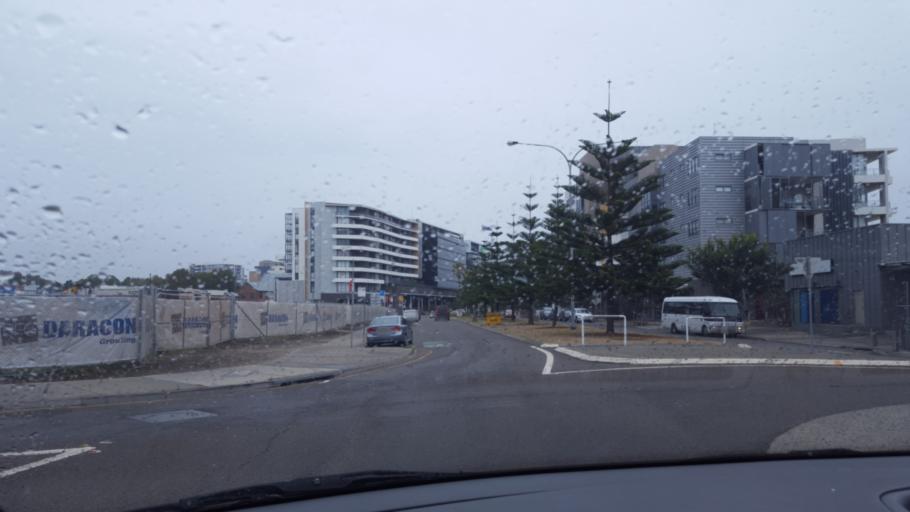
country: AU
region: New South Wales
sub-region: Newcastle
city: Newcastle
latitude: -32.9256
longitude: 151.7698
